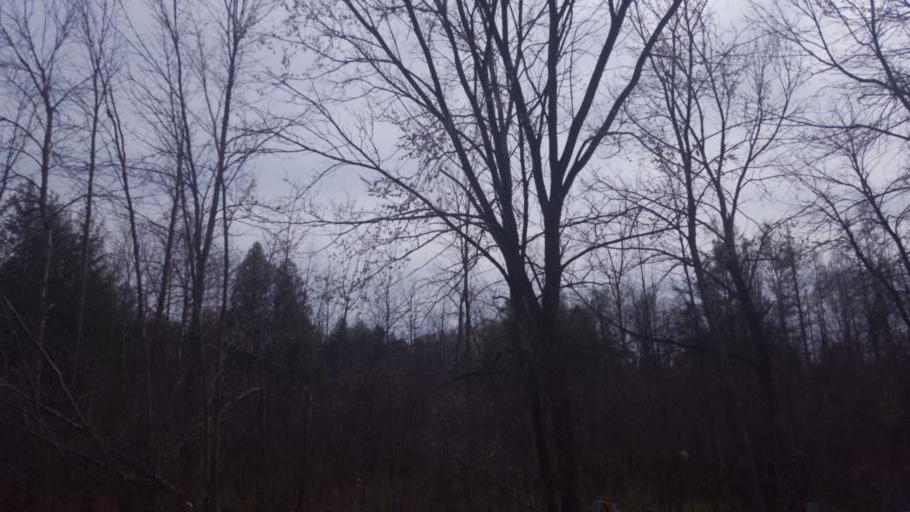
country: US
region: Michigan
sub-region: Clare County
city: Clare
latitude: 43.8727
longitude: -84.7661
